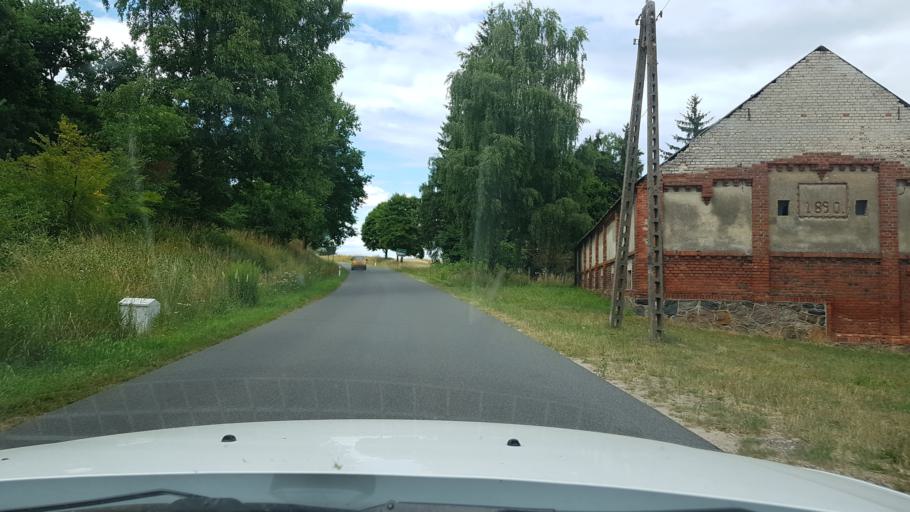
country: PL
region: West Pomeranian Voivodeship
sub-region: Powiat drawski
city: Kalisz Pomorski
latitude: 53.3066
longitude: 15.9187
